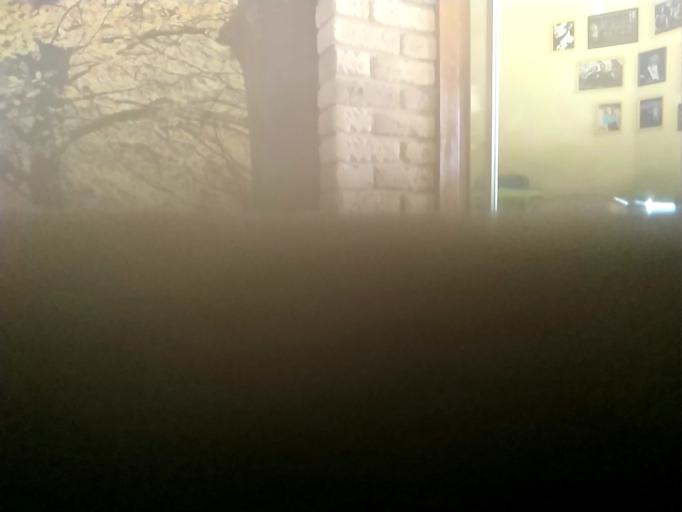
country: RU
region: Kaluga
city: Yukhnov
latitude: 54.7919
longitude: 35.0167
